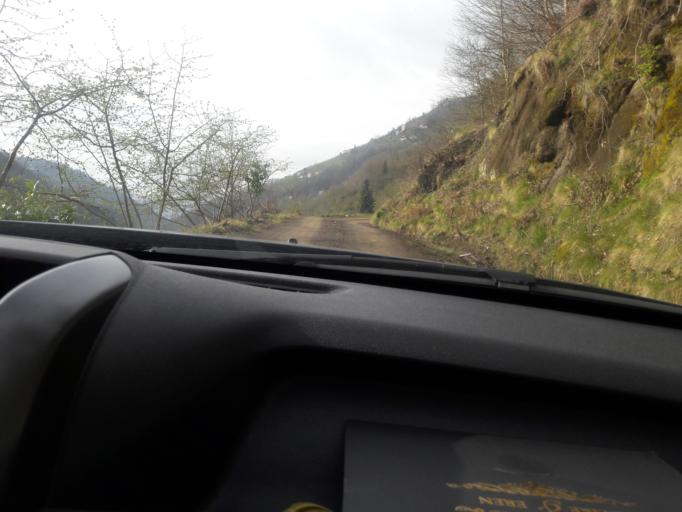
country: TR
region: Trabzon
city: Salpazari
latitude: 40.9698
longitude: 39.1965
